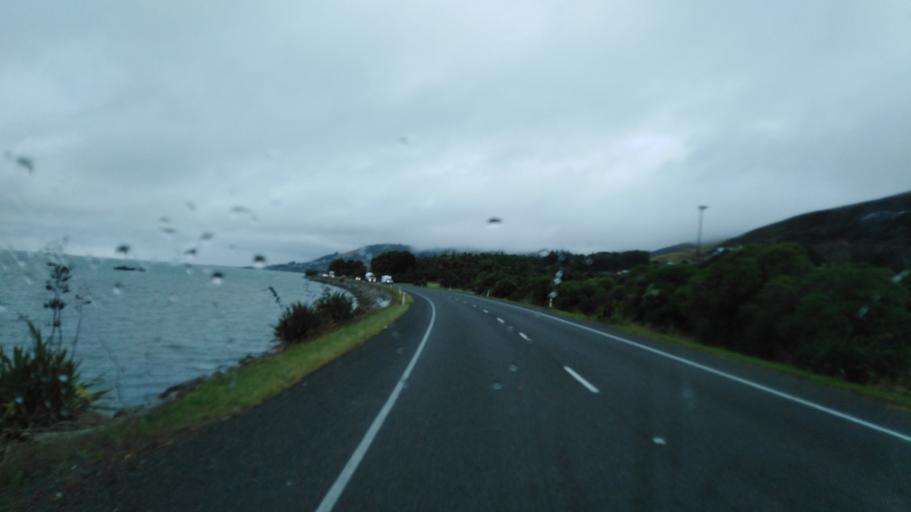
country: NZ
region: Nelson
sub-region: Nelson City
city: Nelson
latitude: -41.2622
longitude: 173.2925
